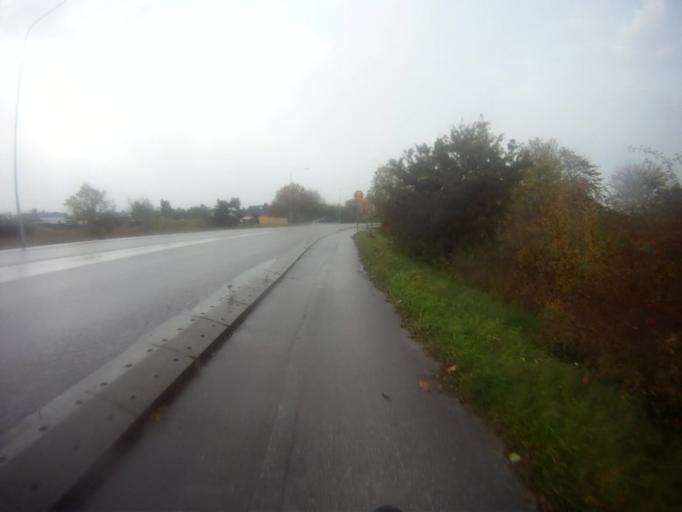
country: SE
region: Gotland
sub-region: Gotland
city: Visby
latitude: 57.6508
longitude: 18.3166
